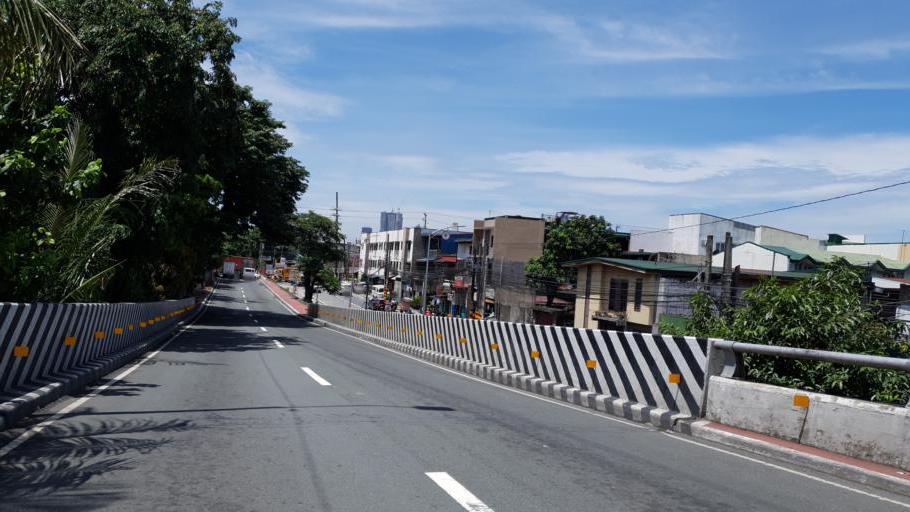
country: PH
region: Metro Manila
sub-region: City of Manila
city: Quiapo
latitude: 14.5876
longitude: 121.0064
